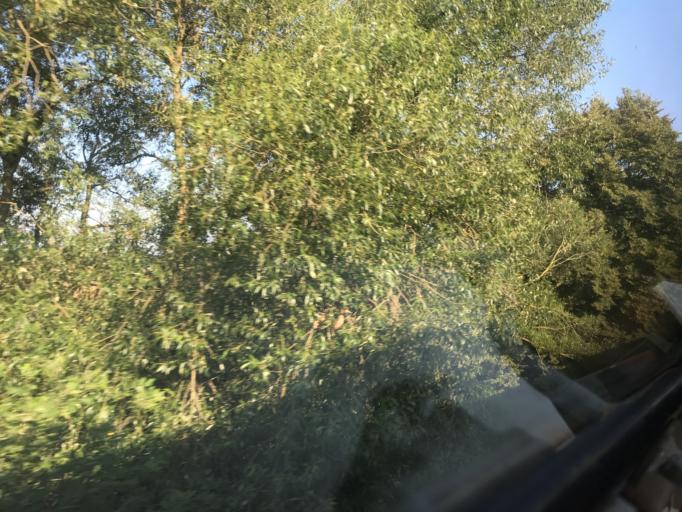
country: CZ
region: Jihocesky
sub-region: Okres Jindrichuv Hradec
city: Lomnice nad Luznici
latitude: 49.0703
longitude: 14.7328
